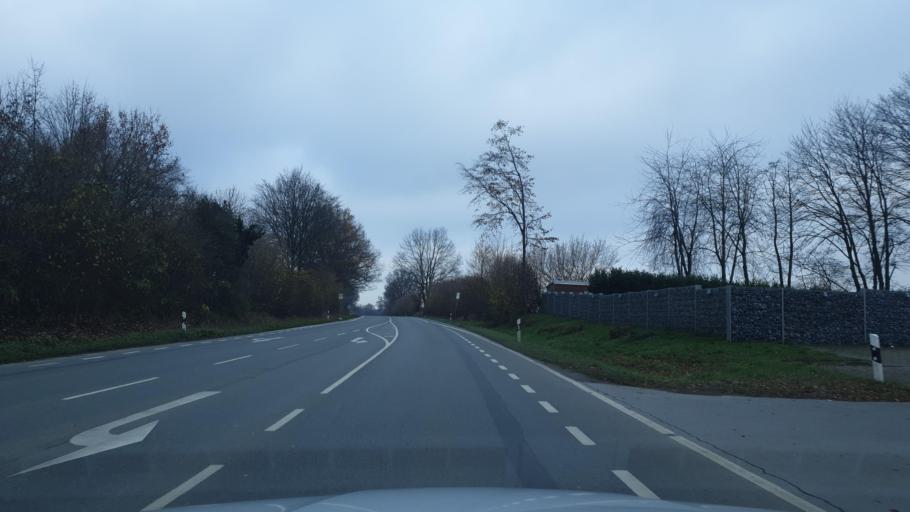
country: DE
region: North Rhine-Westphalia
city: Enger
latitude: 52.0918
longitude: 8.5861
